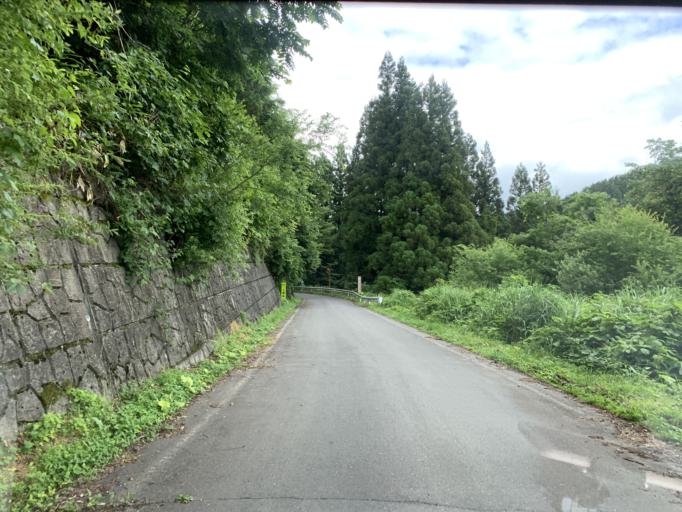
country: JP
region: Iwate
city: Ichinoseki
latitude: 38.9601
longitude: 140.8969
